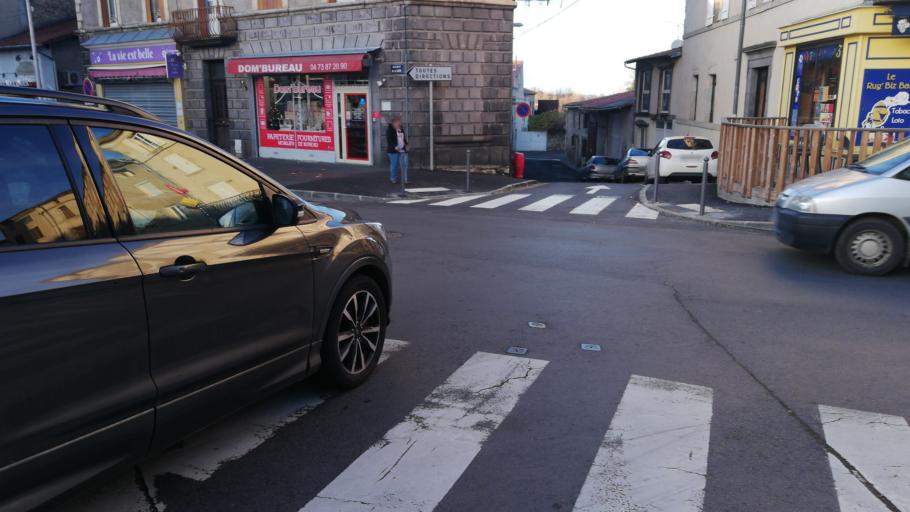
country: FR
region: Auvergne
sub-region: Departement du Puy-de-Dome
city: Billom
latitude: 45.7240
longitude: 3.3377
